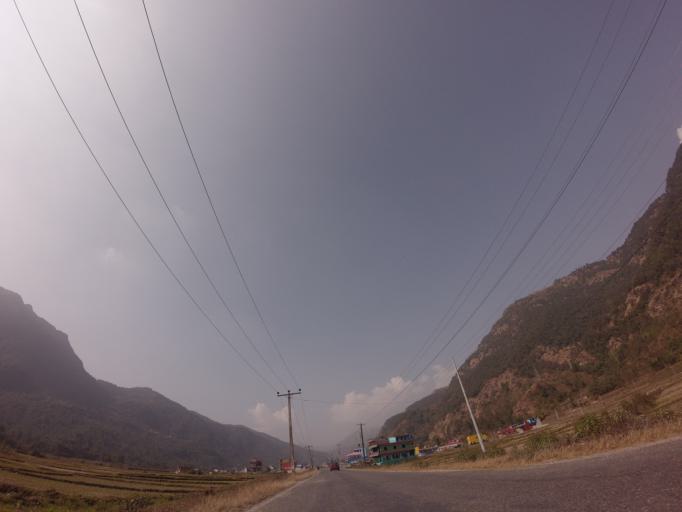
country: NP
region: Western Region
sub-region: Gandaki Zone
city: Pokhara
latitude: 28.2844
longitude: 83.9160
